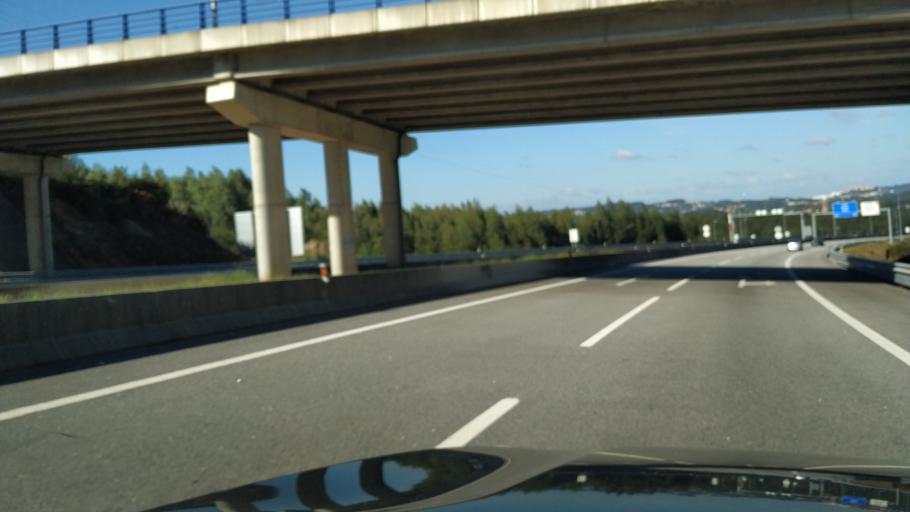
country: PT
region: Porto
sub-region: Vila Nova de Gaia
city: Olival
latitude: 41.0550
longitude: -8.5208
